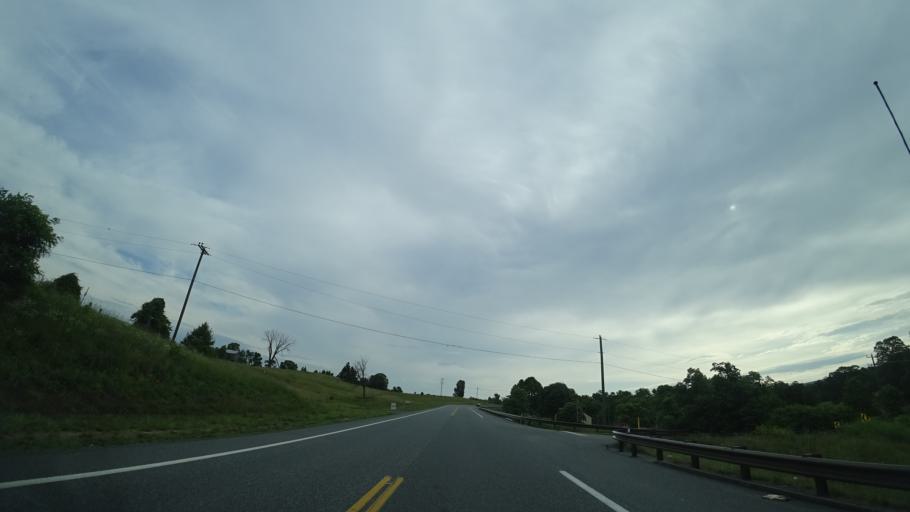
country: US
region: Virginia
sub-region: Page County
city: Luray
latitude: 38.7729
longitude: -78.3812
